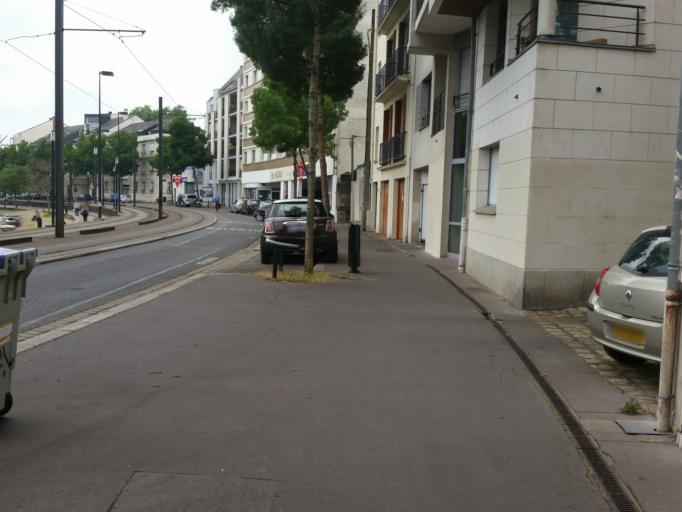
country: FR
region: Pays de la Loire
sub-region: Departement de la Loire-Atlantique
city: Nantes
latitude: 47.2261
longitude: -1.5558
